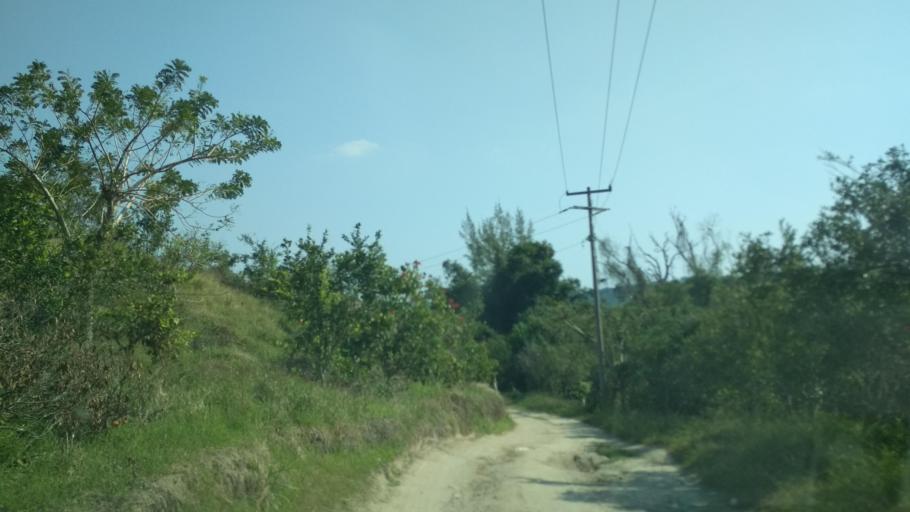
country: MX
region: Puebla
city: San Jose Acateno
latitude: 20.1803
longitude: -97.2573
